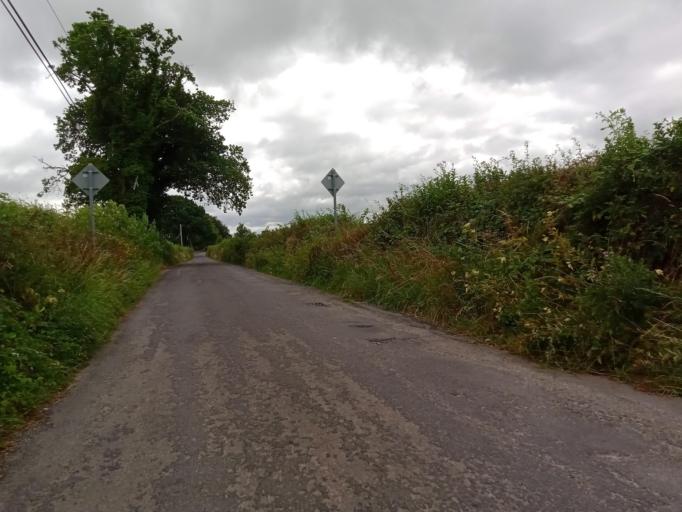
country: IE
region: Leinster
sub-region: Kilkenny
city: Callan
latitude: 52.5749
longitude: -7.3779
